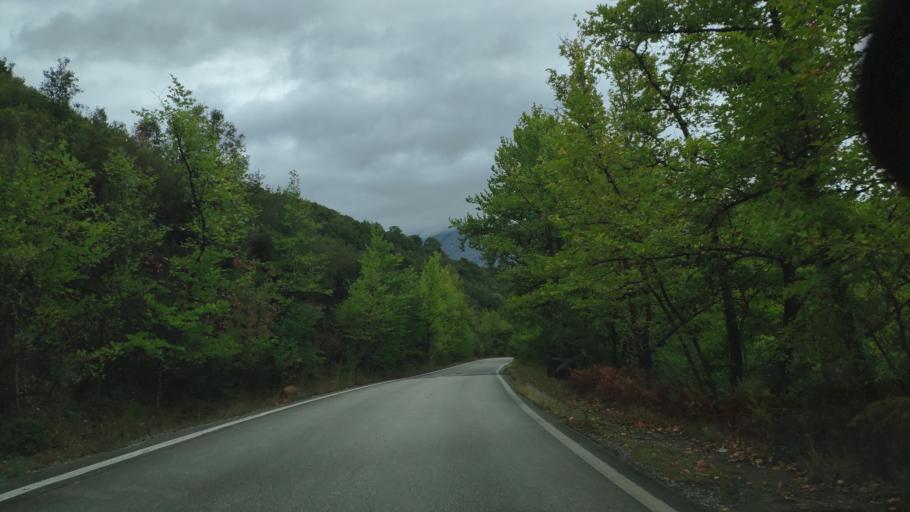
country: GR
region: West Greece
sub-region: Nomos Aitolias kai Akarnanias
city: Sardinia
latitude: 38.9458
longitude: 21.3388
